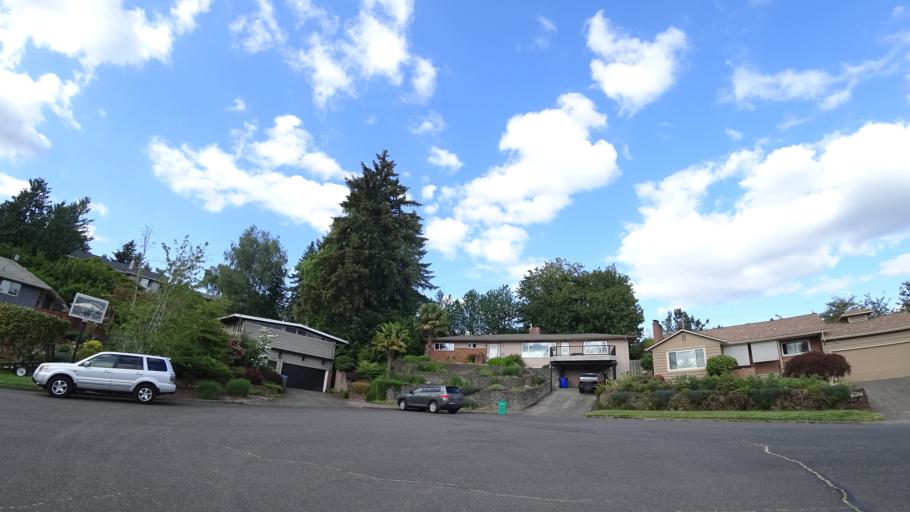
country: US
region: Oregon
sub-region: Washington County
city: Garden Home-Whitford
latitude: 45.4770
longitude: -122.7162
